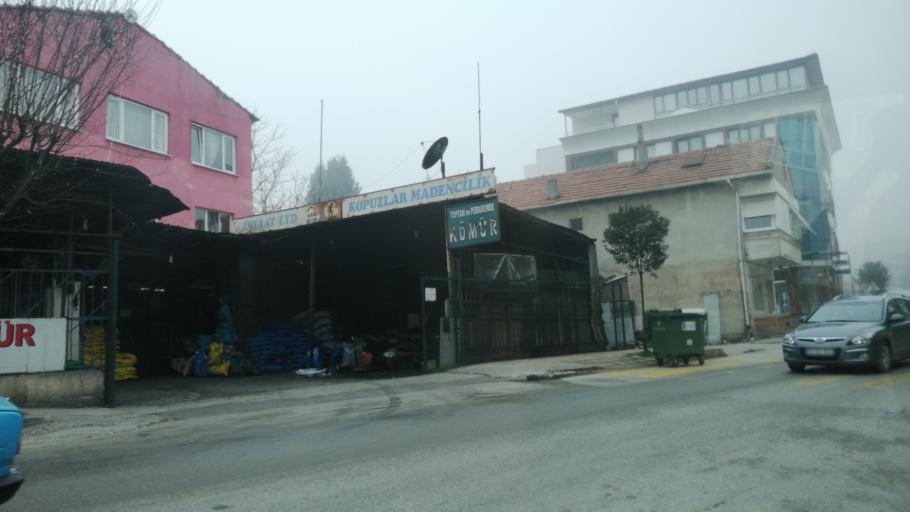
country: TR
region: Yalova
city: Yalova
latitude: 40.6546
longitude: 29.2788
